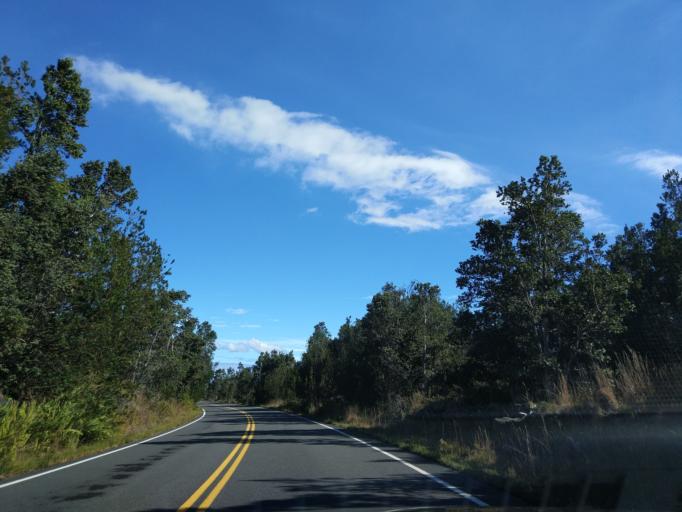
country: US
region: Hawaii
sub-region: Hawaii County
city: Volcano
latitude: 19.3474
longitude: -155.2177
